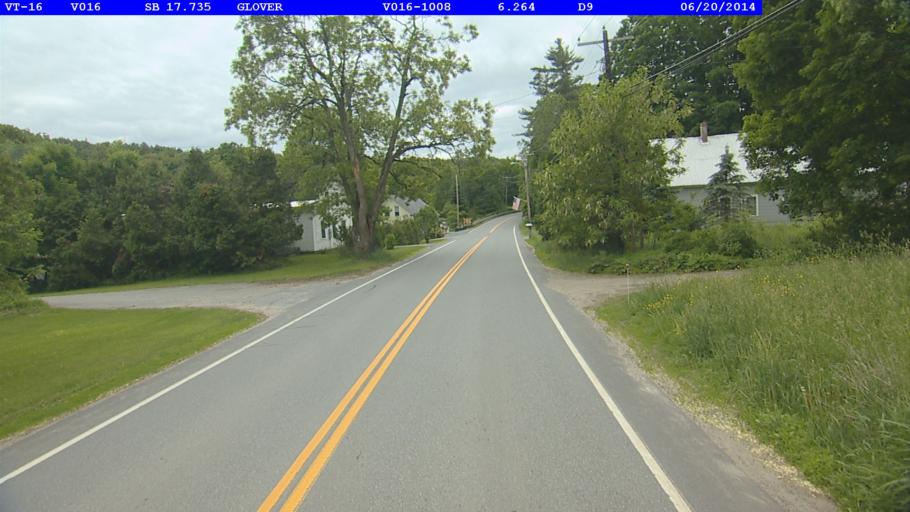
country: US
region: Vermont
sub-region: Orleans County
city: Newport
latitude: 44.7111
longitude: -72.1855
